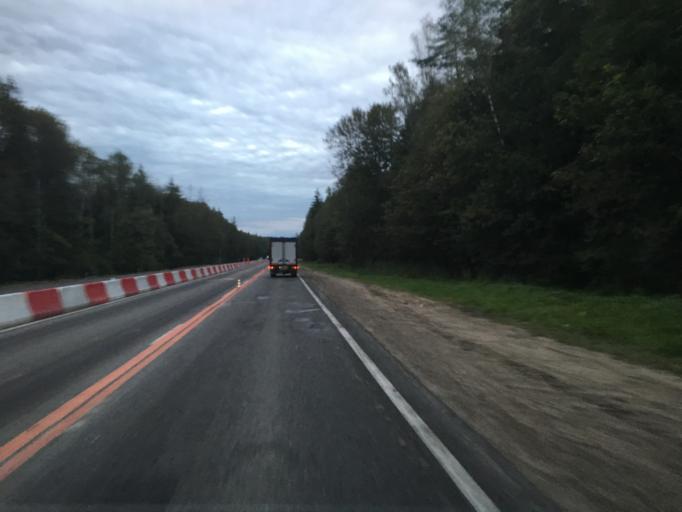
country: RU
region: Kaluga
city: Detchino
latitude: 54.7029
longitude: 36.2920
